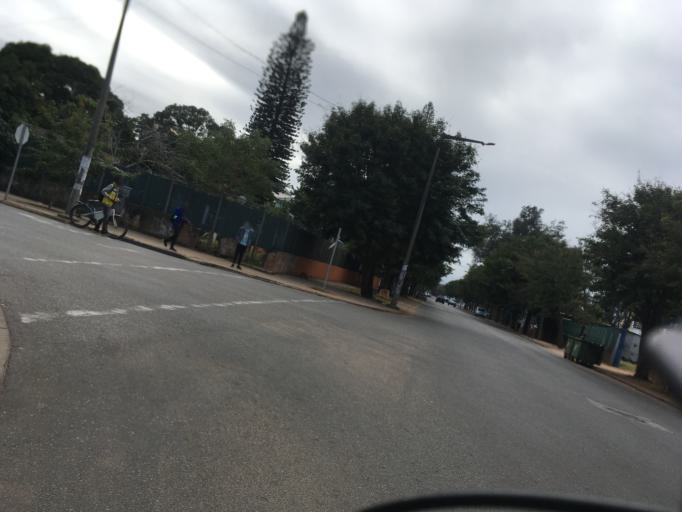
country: MZ
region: Maputo City
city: Maputo
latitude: -25.9679
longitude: 32.5935
